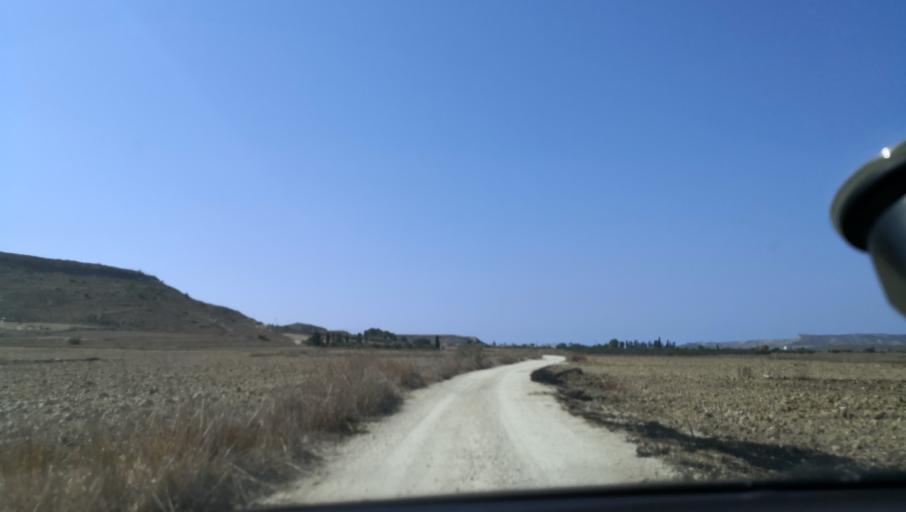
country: CY
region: Lefkosia
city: Mammari
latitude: 35.1764
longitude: 33.2195
